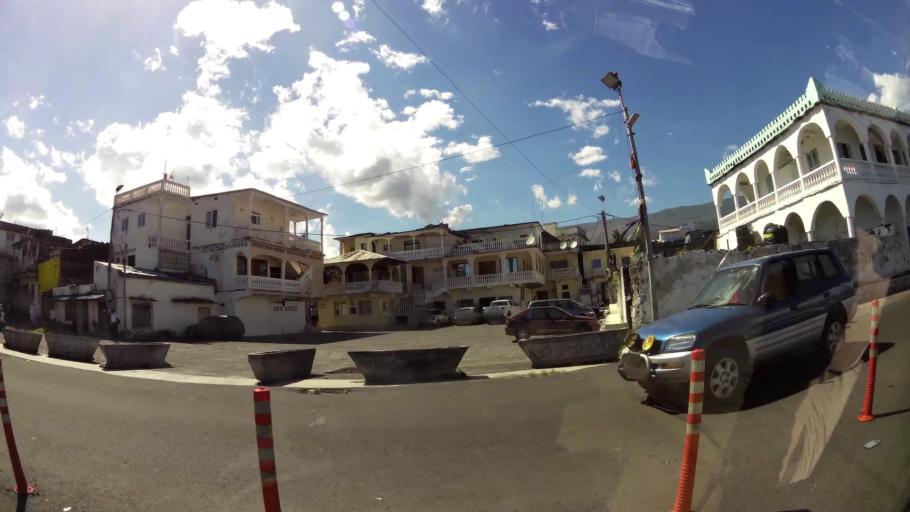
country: KM
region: Grande Comore
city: Moroni
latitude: -11.7029
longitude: 43.2521
